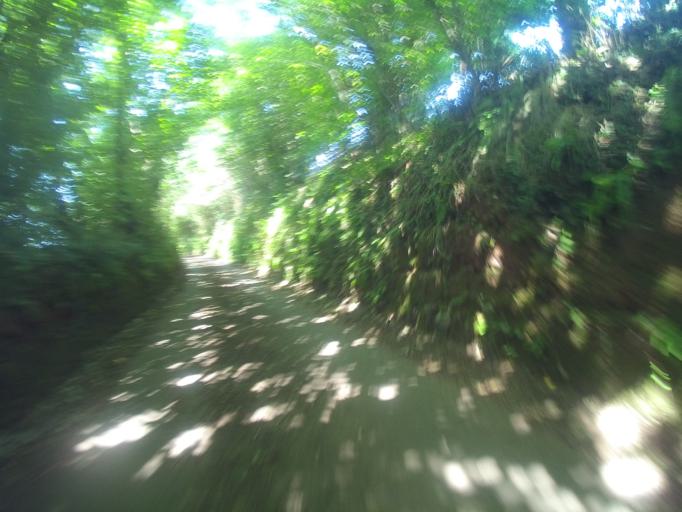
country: GB
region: England
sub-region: Devon
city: Dartmouth
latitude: 50.3615
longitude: -3.6190
